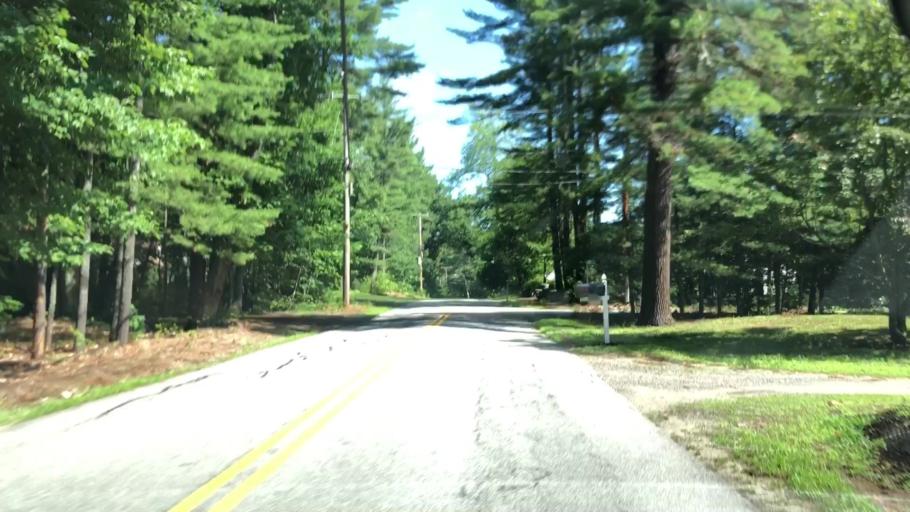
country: US
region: New Hampshire
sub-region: Hillsborough County
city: Milford
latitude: 42.8403
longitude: -71.5956
